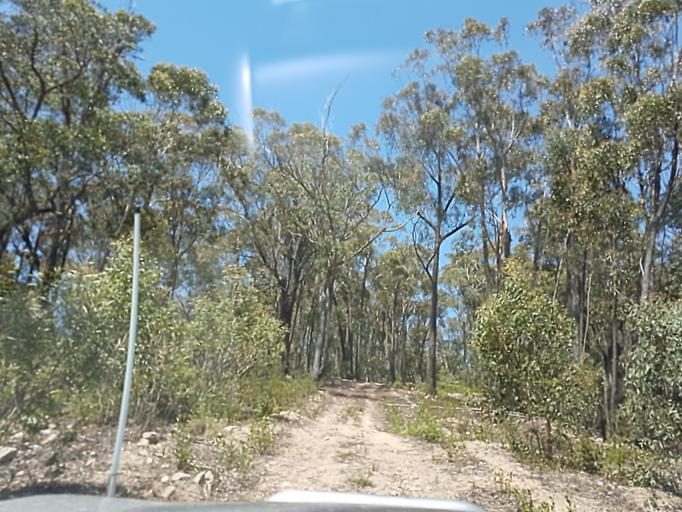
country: AU
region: Victoria
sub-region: East Gippsland
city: Lakes Entrance
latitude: -37.3084
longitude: 148.3600
